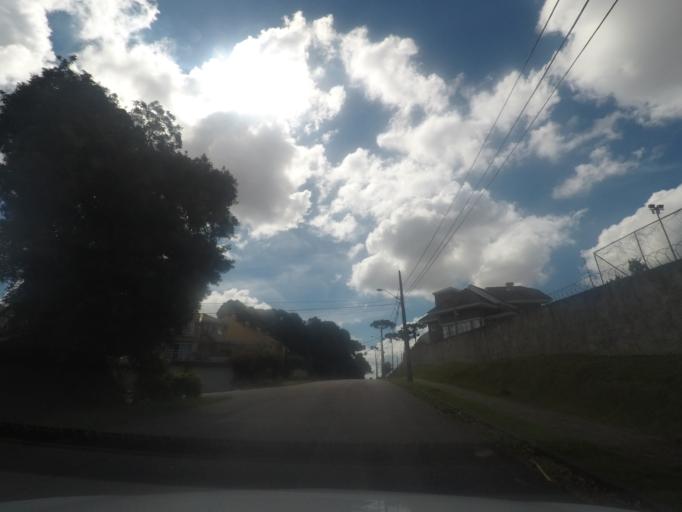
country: BR
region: Parana
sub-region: Pinhais
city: Pinhais
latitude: -25.4764
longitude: -49.2210
